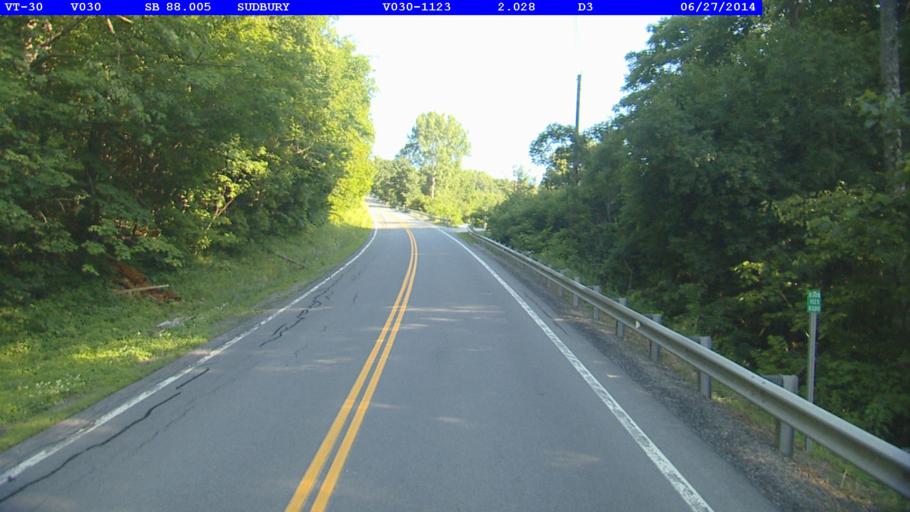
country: US
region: Vermont
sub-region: Rutland County
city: Brandon
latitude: 43.7772
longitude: -73.2037
